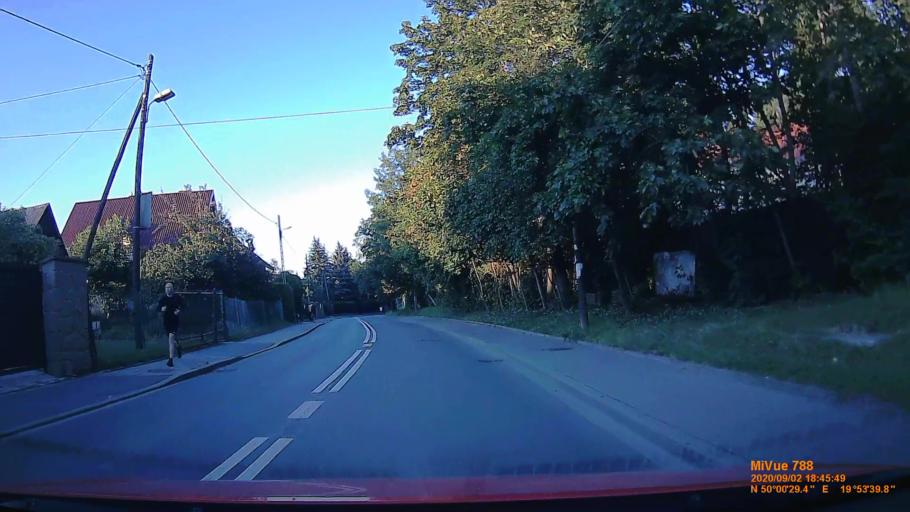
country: PL
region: Lesser Poland Voivodeship
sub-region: Krakow
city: Sidzina
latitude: 50.0083
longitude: 19.8946
